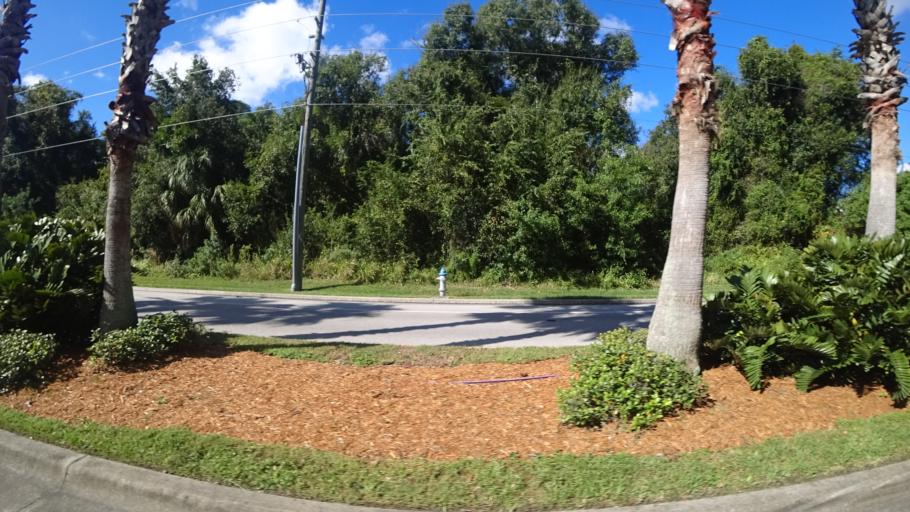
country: US
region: Florida
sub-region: Manatee County
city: Ellenton
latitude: 27.5000
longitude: -82.5019
